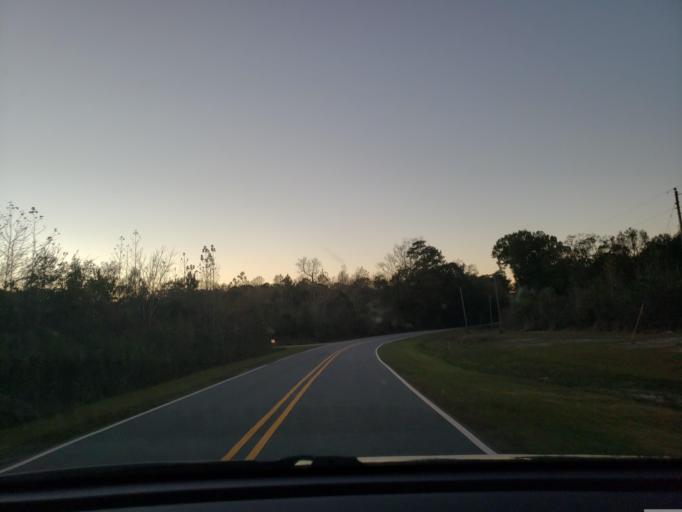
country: US
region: North Carolina
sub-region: Duplin County
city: Beulaville
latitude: 34.7666
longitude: -77.7339
